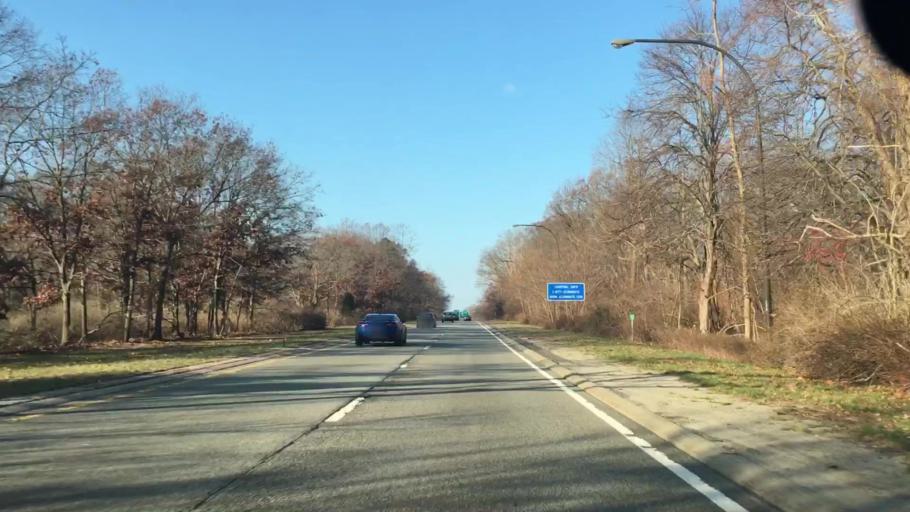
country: US
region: New York
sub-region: Suffolk County
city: Commack
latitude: 40.8179
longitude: -73.2776
